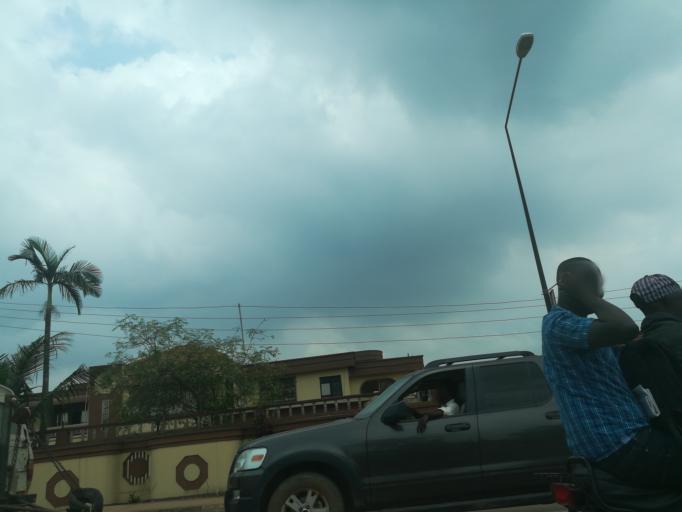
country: NG
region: Lagos
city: Ikorodu
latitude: 6.6155
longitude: 3.5128
